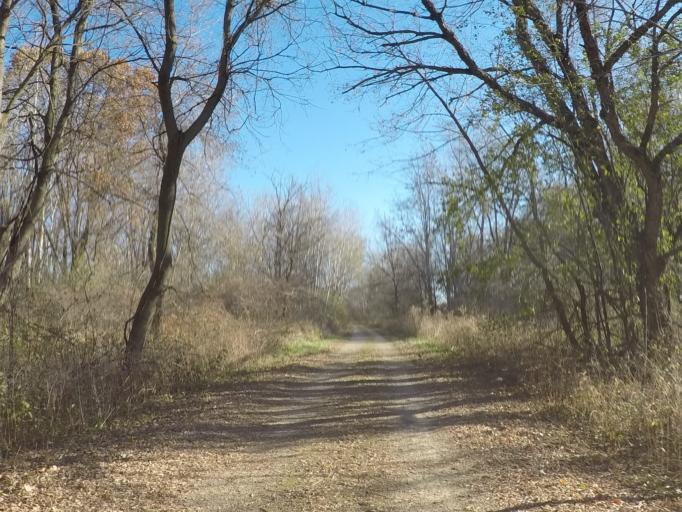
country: US
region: Wisconsin
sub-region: Jefferson County
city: Cambridge
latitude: 43.0442
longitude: -89.0219
